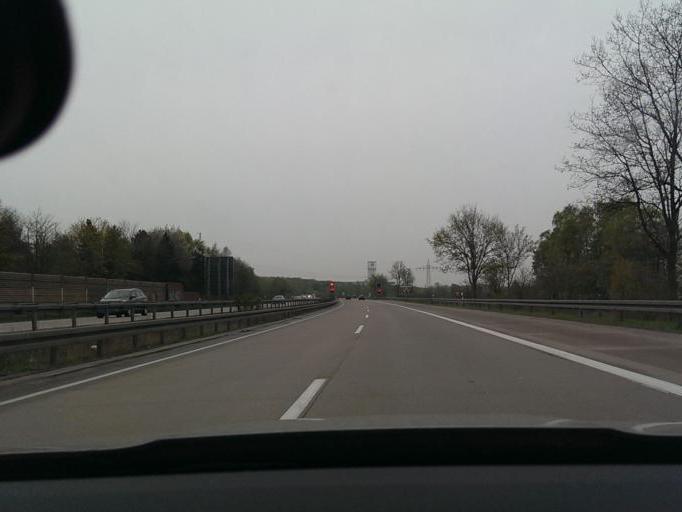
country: DE
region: Lower Saxony
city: Garbsen-Mitte
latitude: 52.4342
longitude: 9.6702
